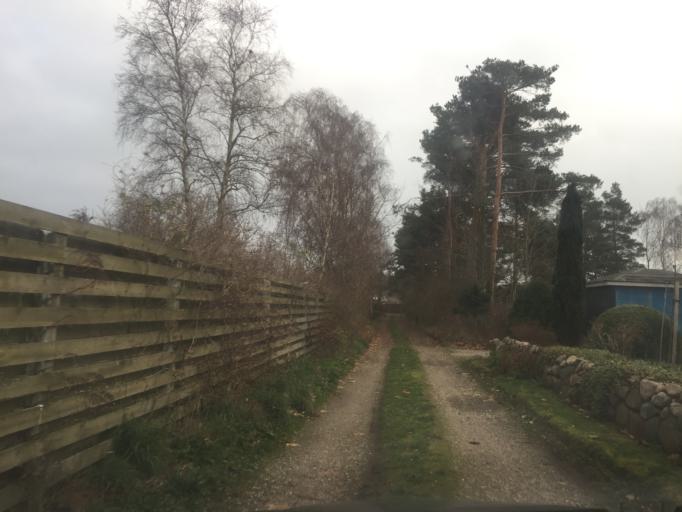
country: DK
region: Capital Region
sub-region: Halsnaes Kommune
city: Liseleje
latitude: 56.0079
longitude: 11.9921
